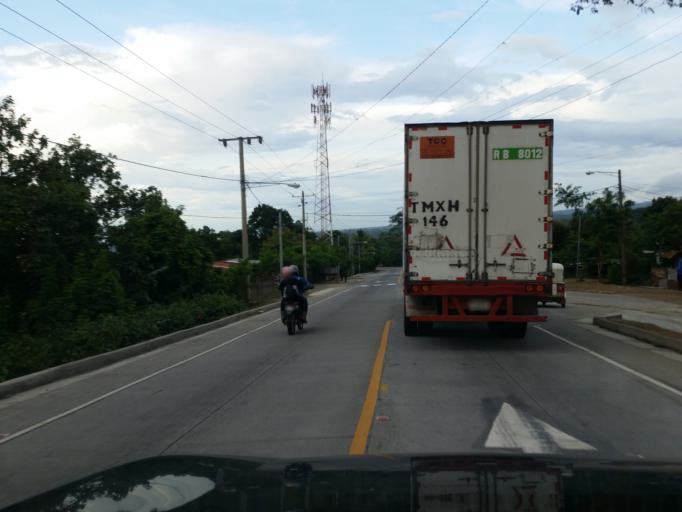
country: NI
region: Managua
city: Ciudad Sandino
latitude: 12.0805
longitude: -86.3683
